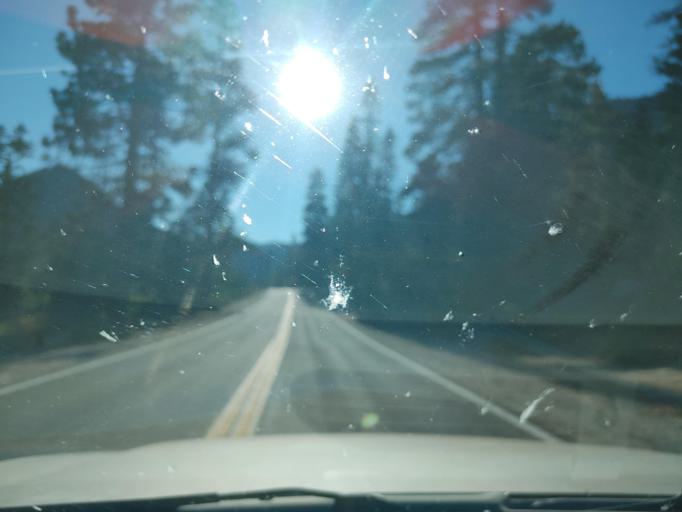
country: US
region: California
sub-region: Placer County
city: Tahoma
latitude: 38.9619
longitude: -120.1013
